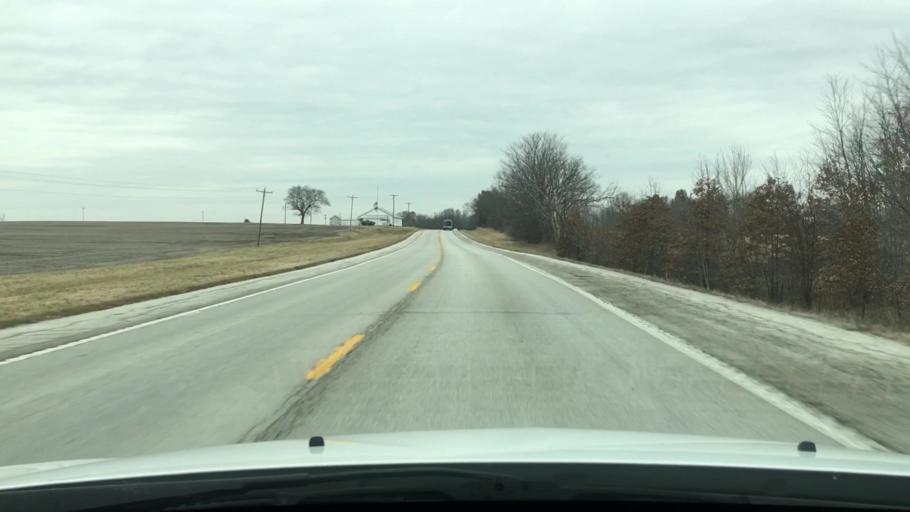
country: US
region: Missouri
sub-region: Montgomery County
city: Wellsville
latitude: 39.2027
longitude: -91.6463
